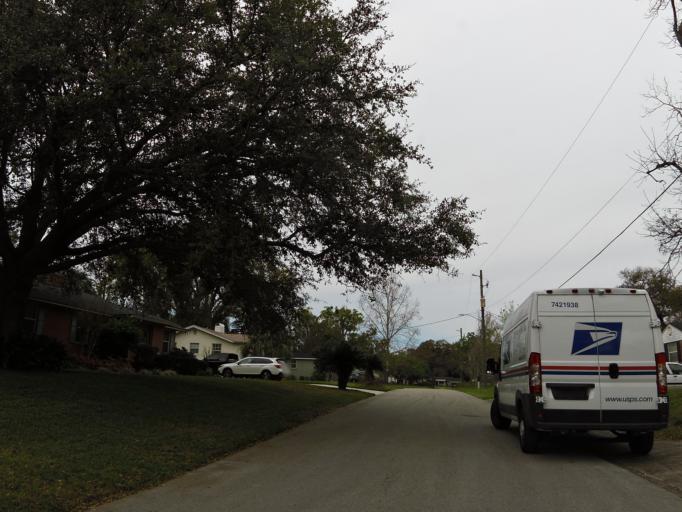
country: US
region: Florida
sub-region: Duval County
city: Jacksonville
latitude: 30.2746
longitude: -81.6477
